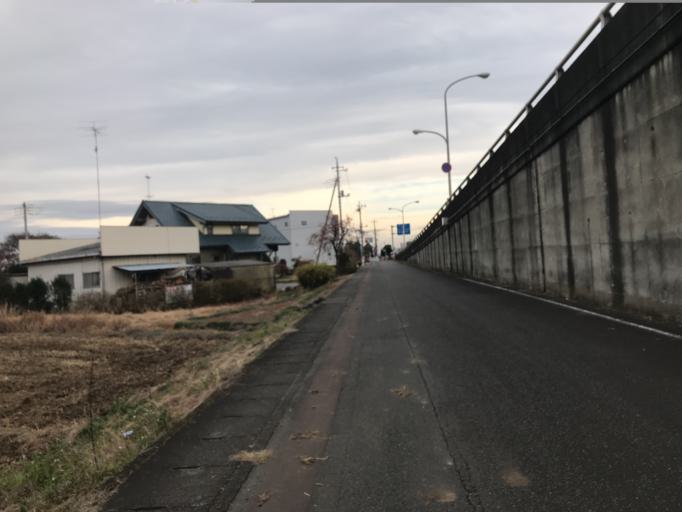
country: JP
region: Gunma
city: Ota
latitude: 36.3034
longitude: 139.3979
